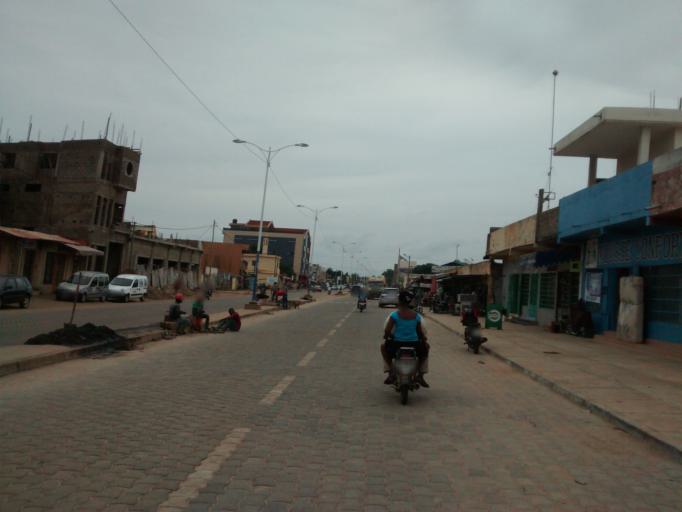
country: TG
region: Maritime
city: Lome
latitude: 6.1773
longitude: 1.1970
